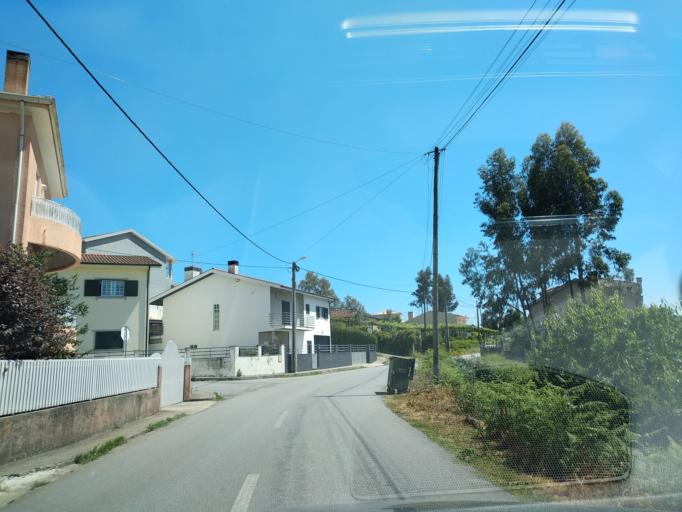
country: PT
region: Porto
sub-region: Paredes
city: Gandra
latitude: 41.1834
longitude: -8.4231
